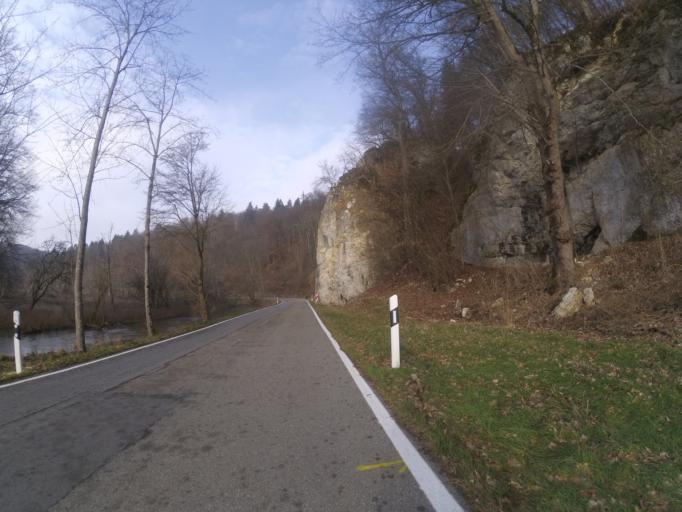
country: DE
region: Baden-Wuerttemberg
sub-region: Tuebingen Region
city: Lauterach
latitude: 48.2598
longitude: 9.5740
